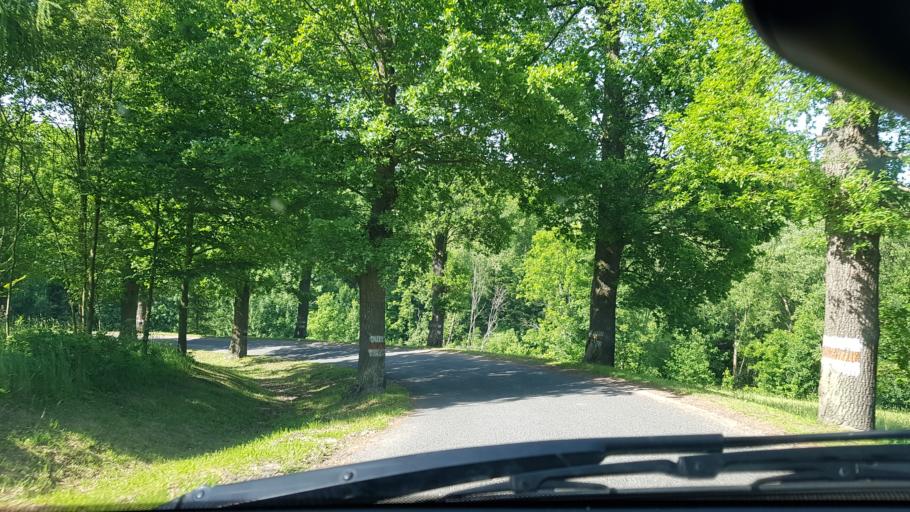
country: PL
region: Lower Silesian Voivodeship
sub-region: Powiat zabkowicki
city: Bardo
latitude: 50.5213
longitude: 16.6595
